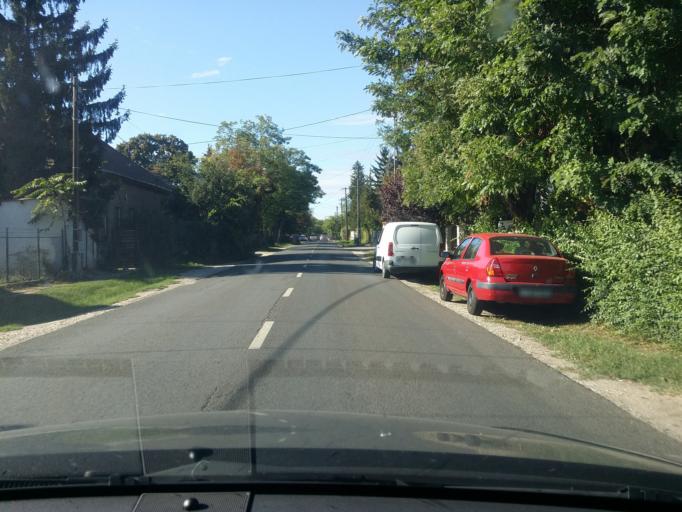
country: HU
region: Pest
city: God
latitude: 47.7017
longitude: 19.1489
